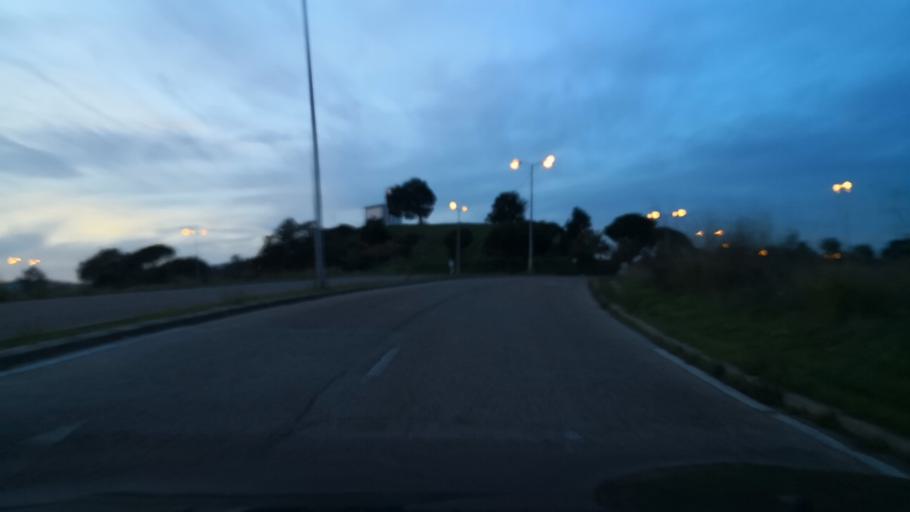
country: PT
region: Setubal
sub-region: Setubal
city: Setubal
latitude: 38.5172
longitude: -8.8615
